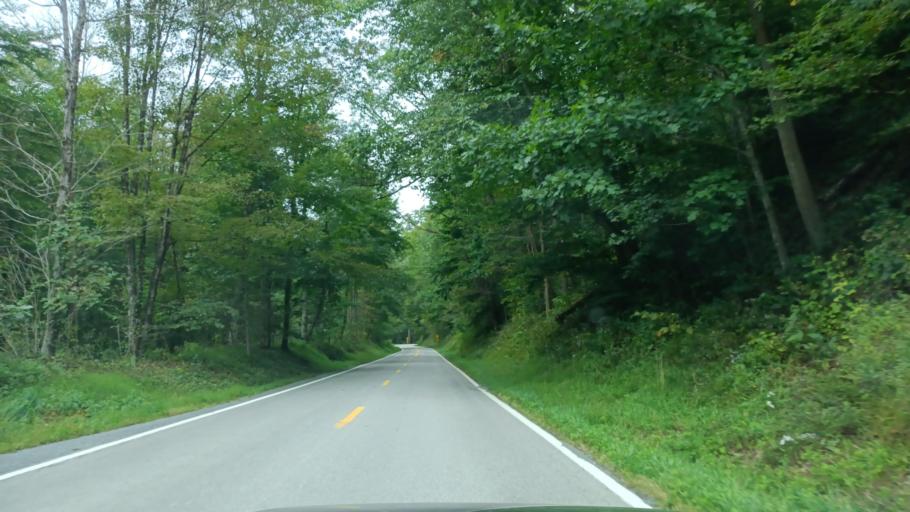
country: US
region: West Virginia
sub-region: Preston County
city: Kingwood
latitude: 39.3192
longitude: -79.7058
